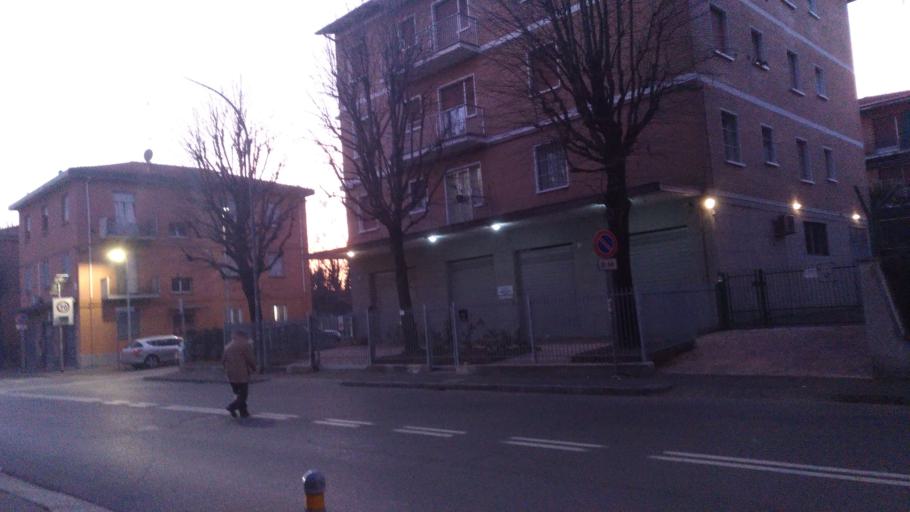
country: IT
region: Emilia-Romagna
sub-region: Provincia di Bologna
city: Bologna
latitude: 44.5248
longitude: 11.3452
